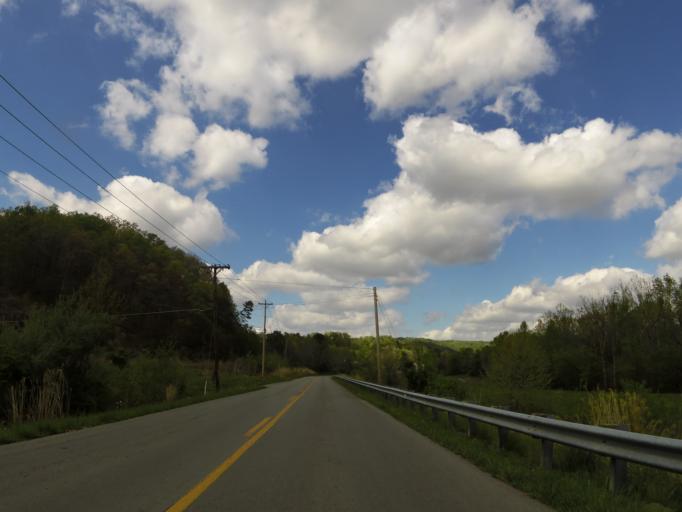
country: US
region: Kentucky
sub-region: Bell County
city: Middlesboro
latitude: 36.6257
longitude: -83.7355
